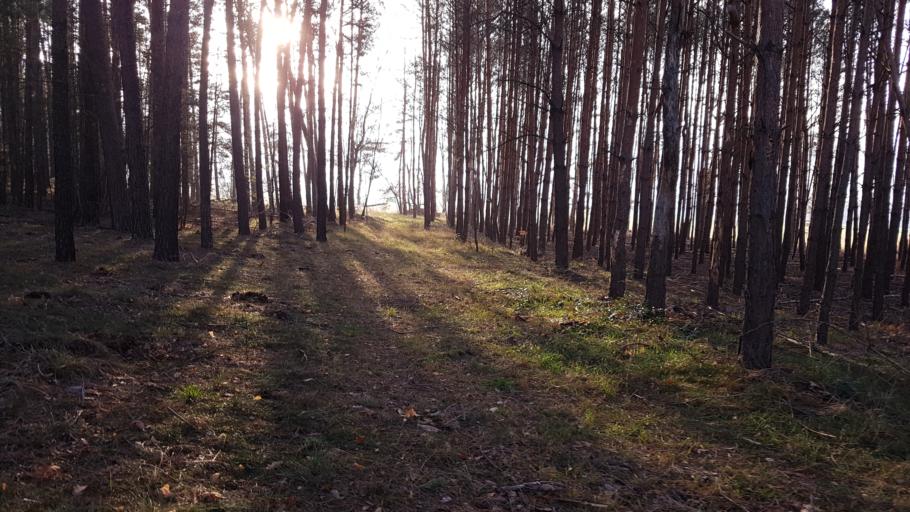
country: DE
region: Brandenburg
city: Schilda
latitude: 51.5815
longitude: 13.3871
